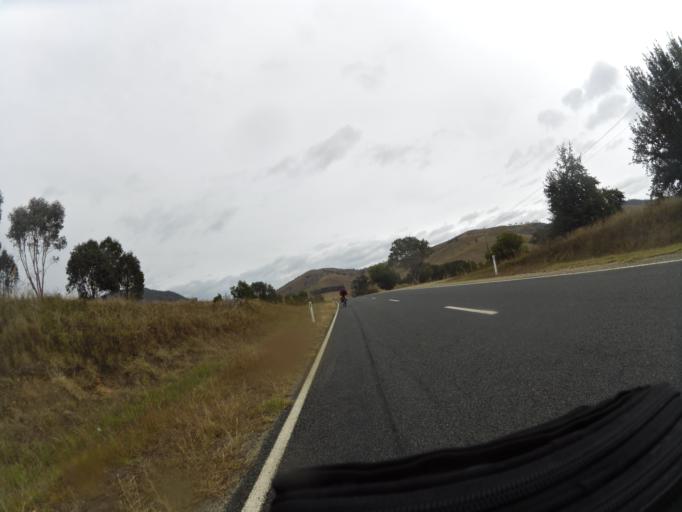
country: AU
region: New South Wales
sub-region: Greater Hume Shire
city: Holbrook
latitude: -36.2036
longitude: 147.7456
